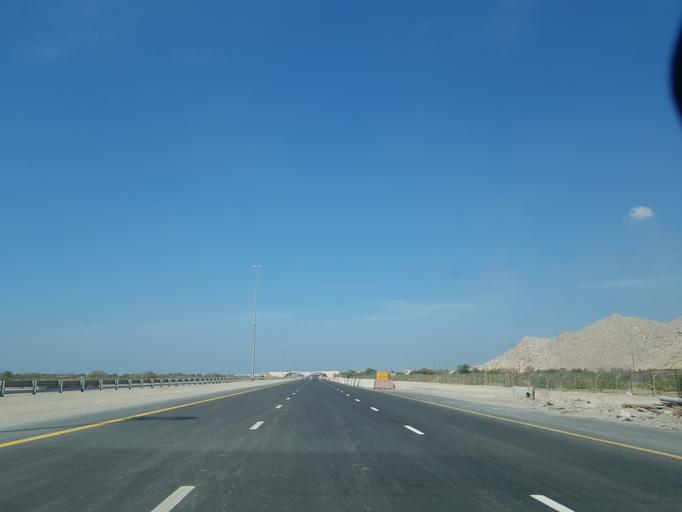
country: AE
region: Ra's al Khaymah
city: Ras al-Khaimah
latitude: 25.8133
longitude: 56.0281
